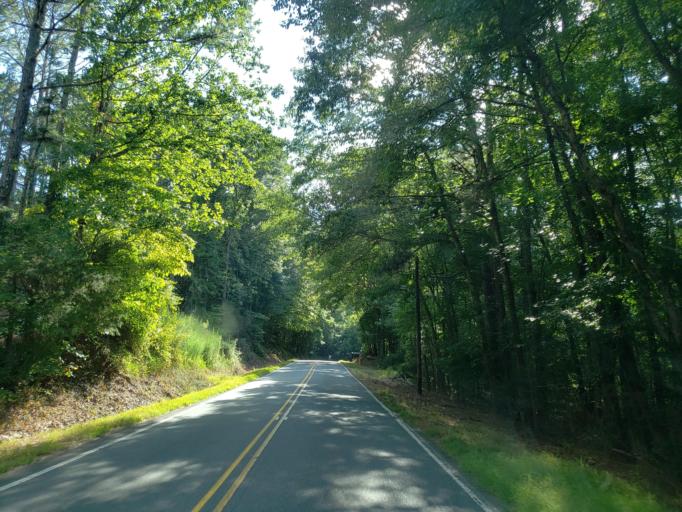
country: US
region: Georgia
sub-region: Floyd County
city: Lindale
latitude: 34.1945
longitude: -85.0721
